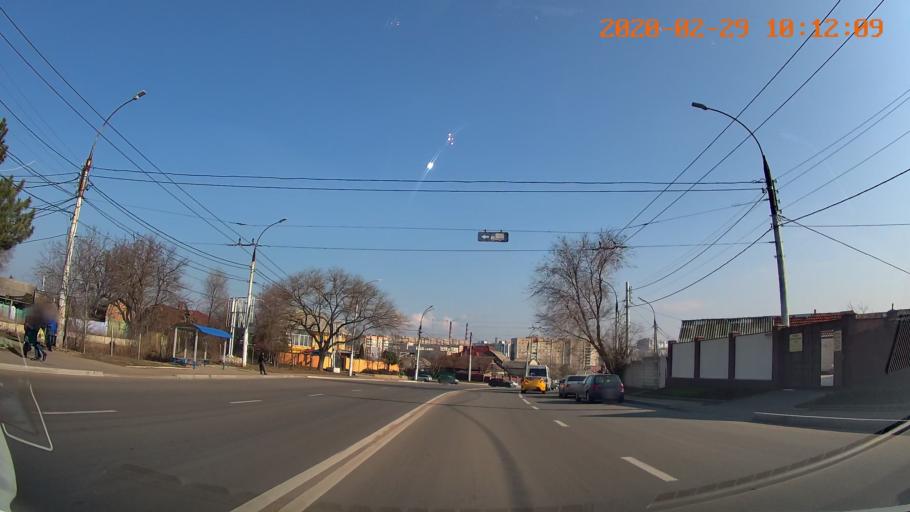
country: MD
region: Telenesti
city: Tiraspolul Nou
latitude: 46.8375
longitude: 29.6468
